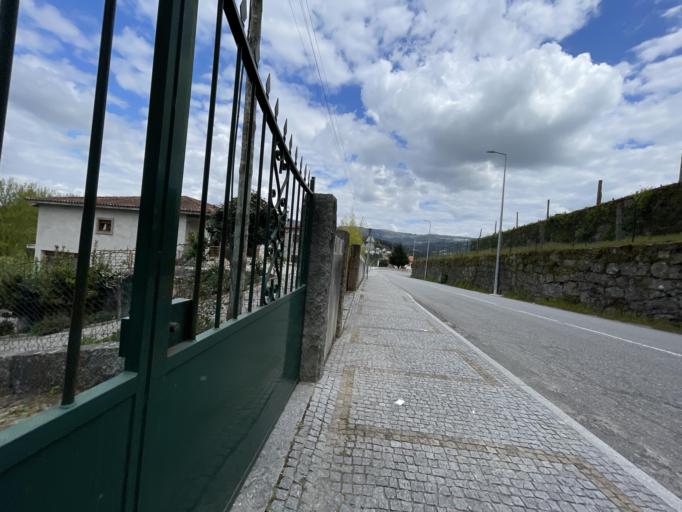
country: PT
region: Porto
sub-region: Marco de Canaveses
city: Marco de Canavezes
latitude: 41.1817
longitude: -8.1413
